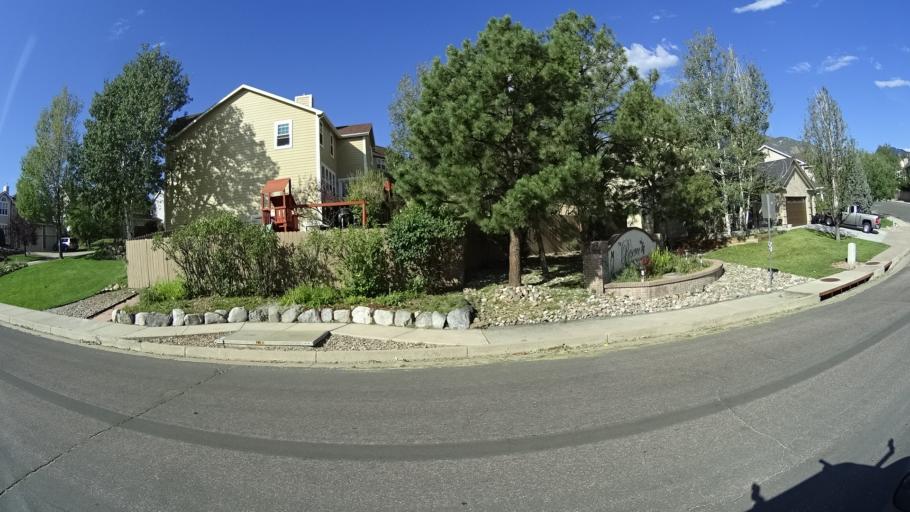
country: US
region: Colorado
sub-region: El Paso County
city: Fort Carson
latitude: 38.7614
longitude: -104.8162
